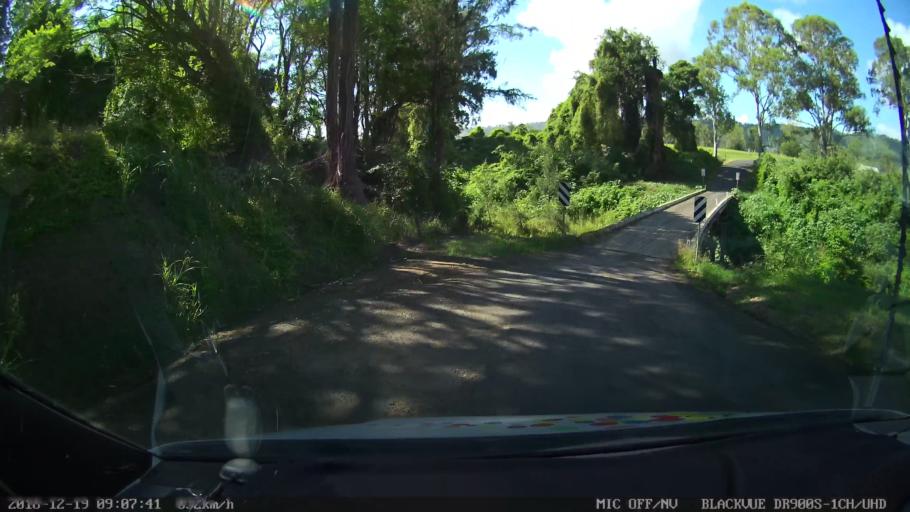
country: AU
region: New South Wales
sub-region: Kyogle
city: Kyogle
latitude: -28.4768
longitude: 152.9331
